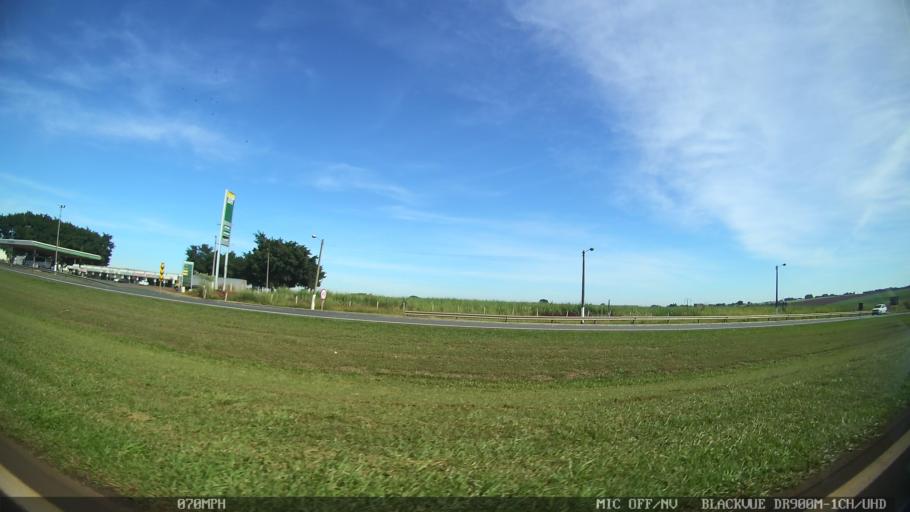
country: BR
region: Sao Paulo
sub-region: Cordeiropolis
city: Cordeiropolis
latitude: -22.4853
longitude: -47.3993
